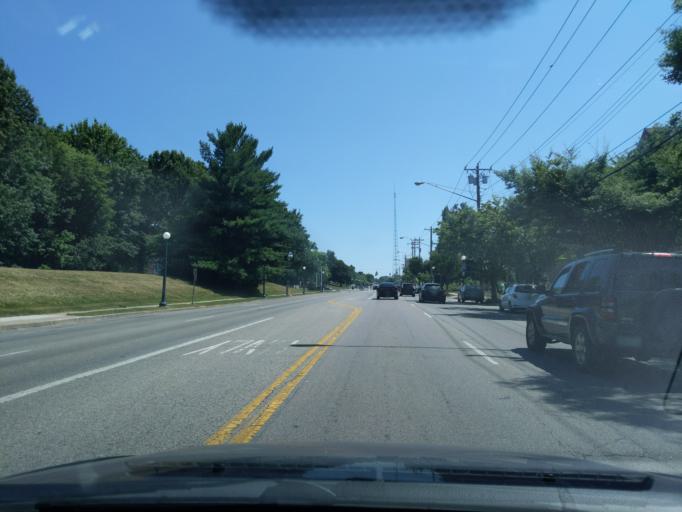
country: US
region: Ohio
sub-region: Hamilton County
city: Saint Bernard
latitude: 39.1371
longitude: -84.5199
